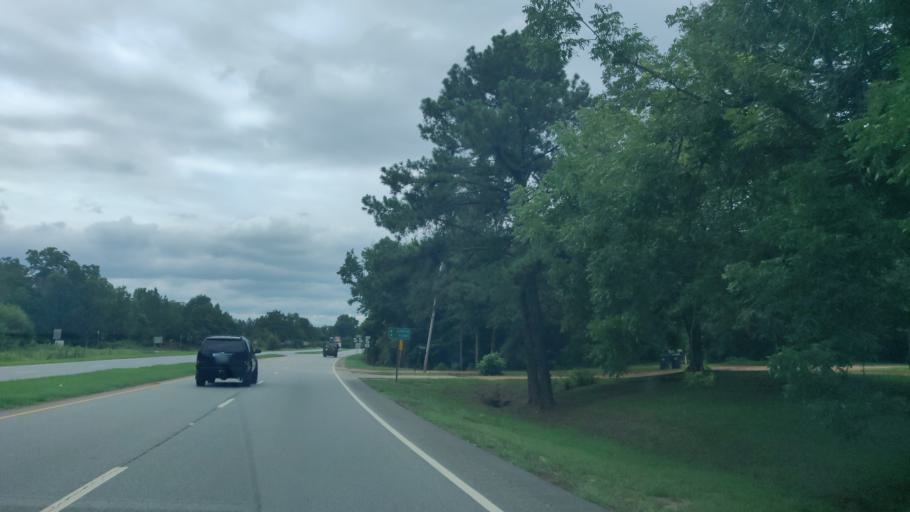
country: US
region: Georgia
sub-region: Terrell County
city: Dawson
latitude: 31.7979
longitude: -84.4477
